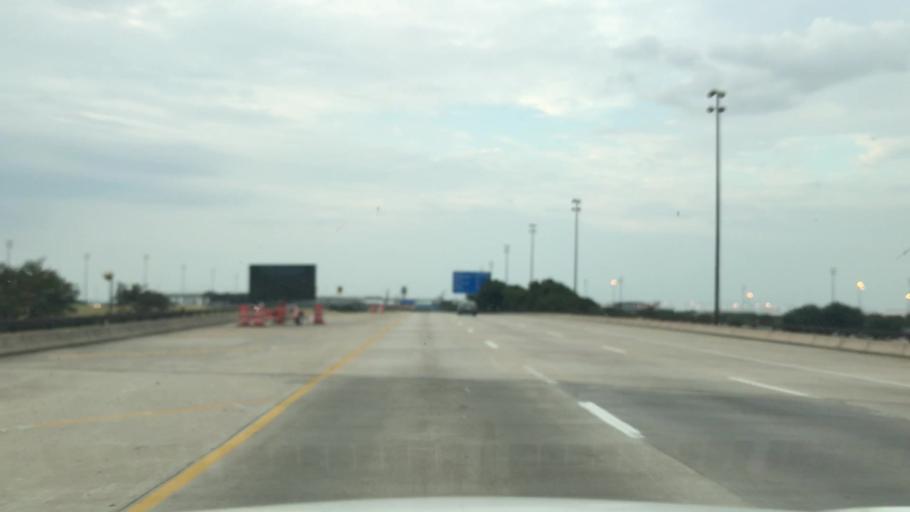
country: US
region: Texas
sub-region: Tarrant County
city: Euless
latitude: 32.8767
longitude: -97.0399
